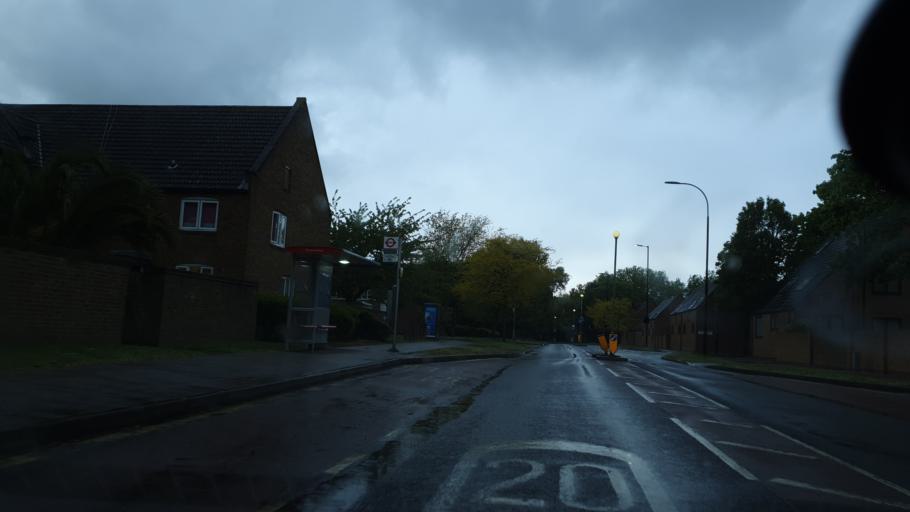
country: GB
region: England
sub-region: Greater London
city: Poplar
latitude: 51.5028
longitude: -0.0358
